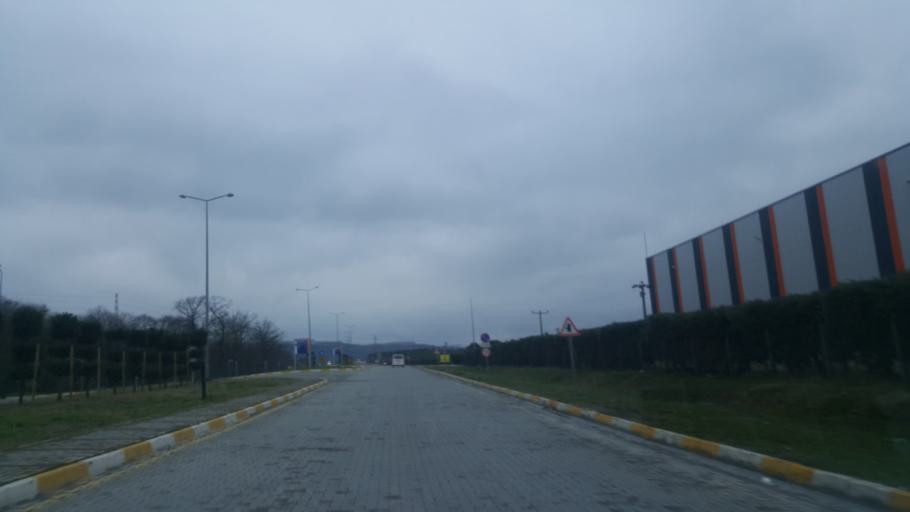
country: TR
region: Kocaeli
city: Mollafeneri
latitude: 40.8687
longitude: 29.5595
